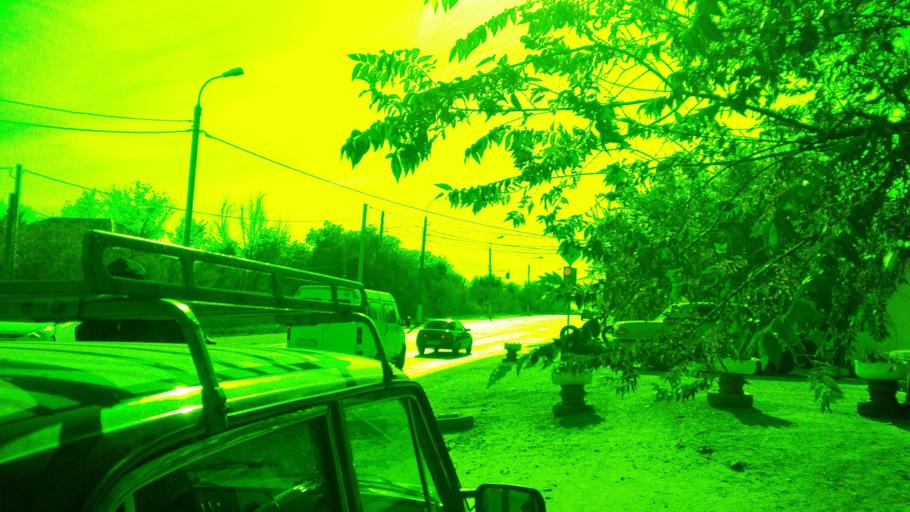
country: RU
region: Volgograd
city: Vodstroy
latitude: 48.8363
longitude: 44.6458
